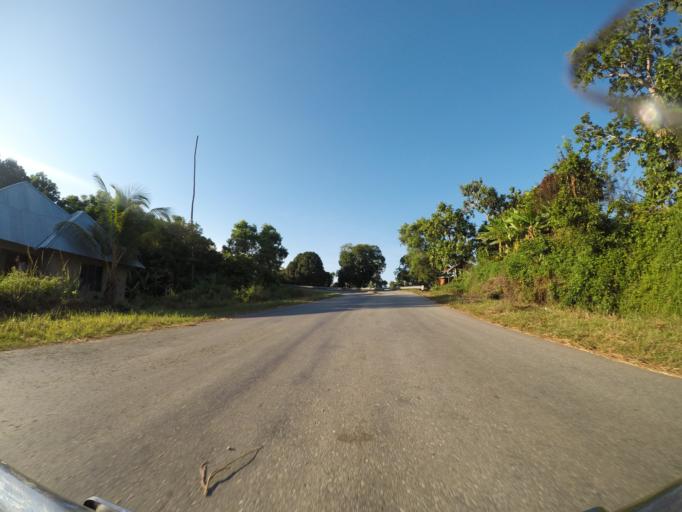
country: TZ
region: Pemba South
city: Mtambile
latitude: -5.3788
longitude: 39.6808
